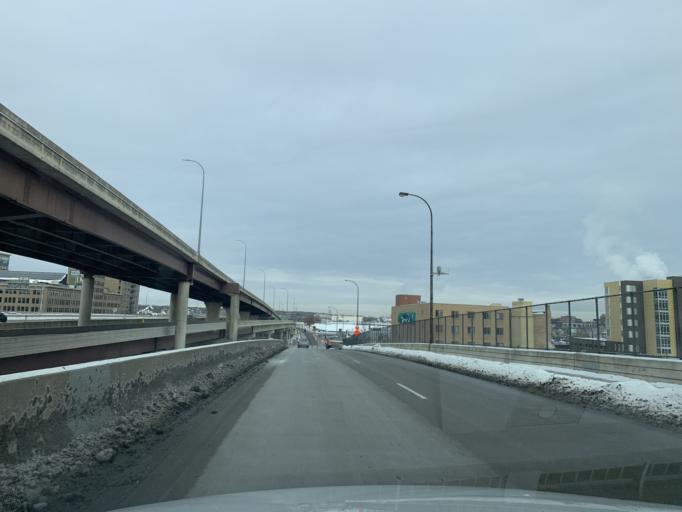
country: US
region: Minnesota
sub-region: Hennepin County
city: Minneapolis
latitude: 44.9776
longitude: -93.2868
